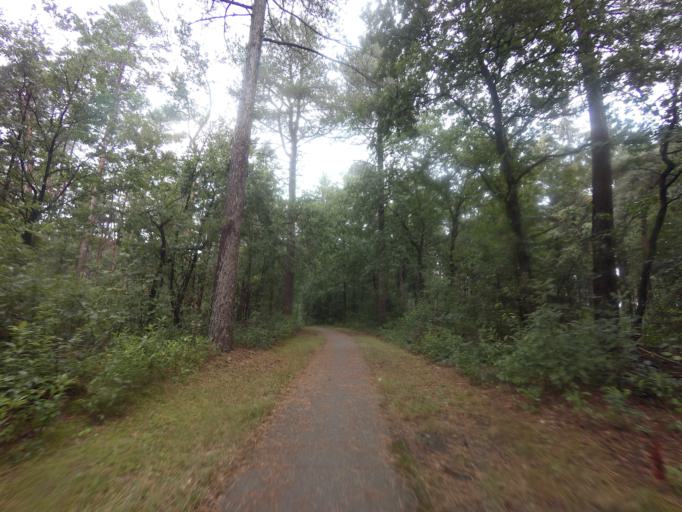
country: NL
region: Overijssel
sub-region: Gemeente Staphorst
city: Staphorst
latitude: 52.6196
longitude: 6.3093
